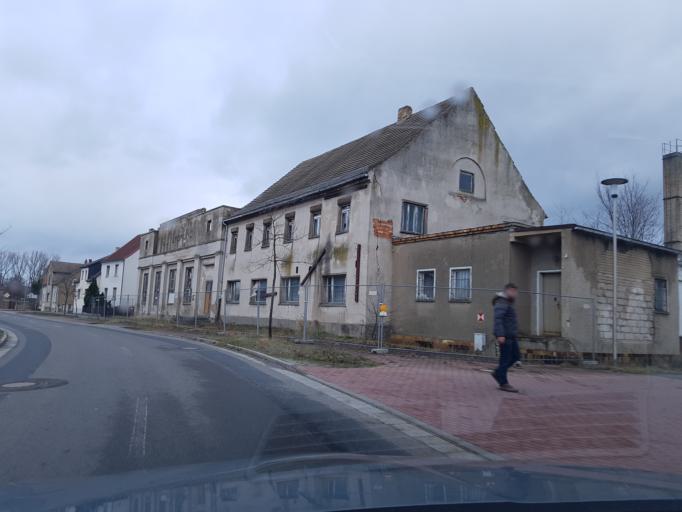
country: DE
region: Brandenburg
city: Bad Liebenwerda
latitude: 51.4798
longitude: 13.4250
